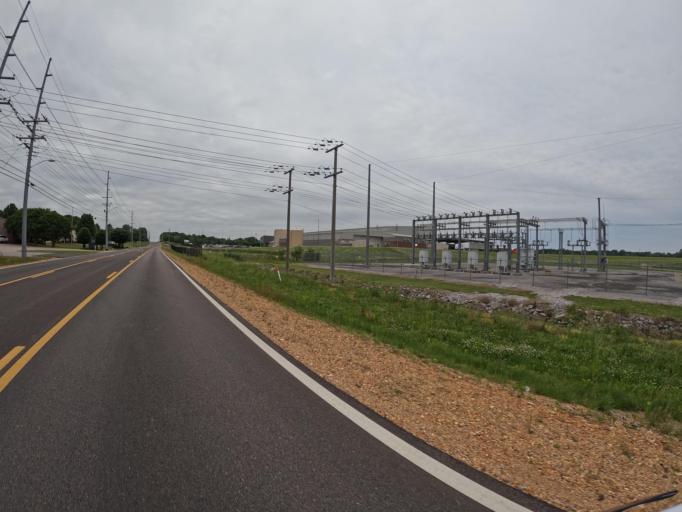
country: US
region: Mississippi
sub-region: Lee County
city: Tupelo
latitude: 34.2743
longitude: -88.7643
